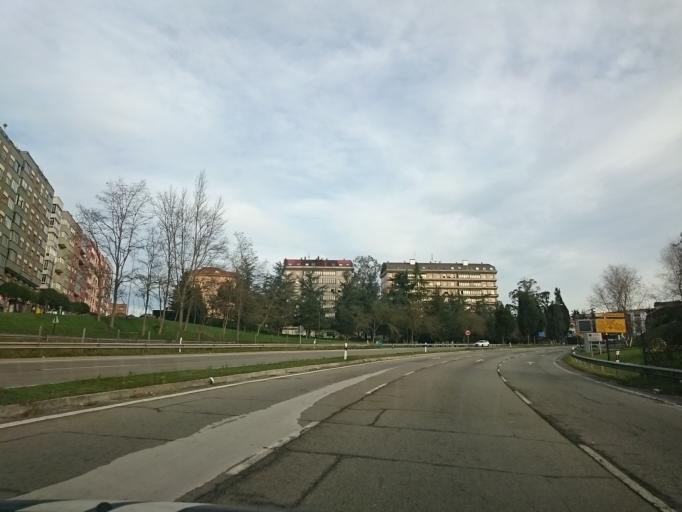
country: ES
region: Asturias
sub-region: Province of Asturias
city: Oviedo
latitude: 43.3540
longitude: -5.8562
